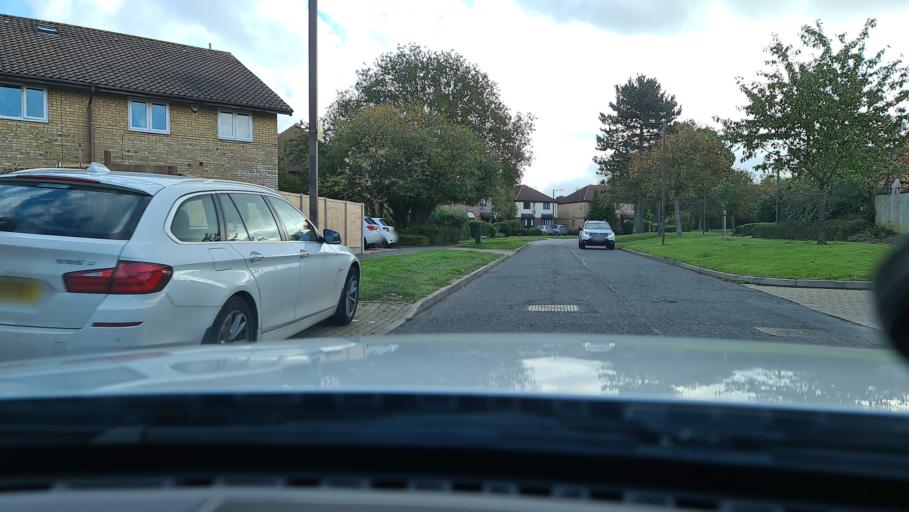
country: GB
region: England
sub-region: Milton Keynes
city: Simpson
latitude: 52.0228
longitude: -0.6942
